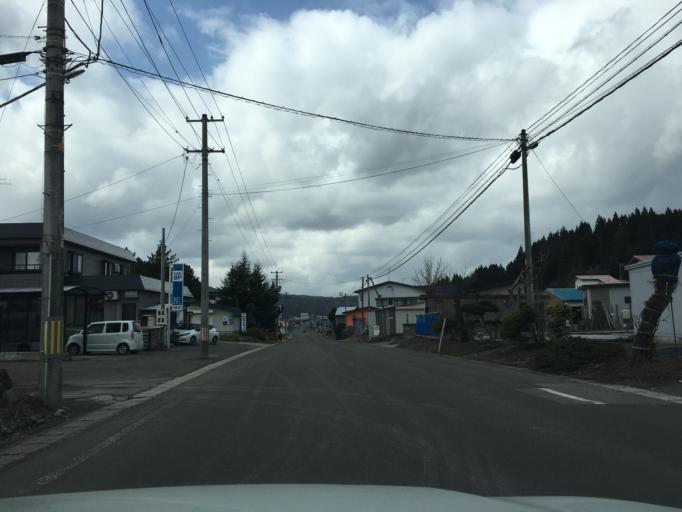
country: JP
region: Akita
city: Takanosu
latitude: 40.1627
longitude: 140.3253
